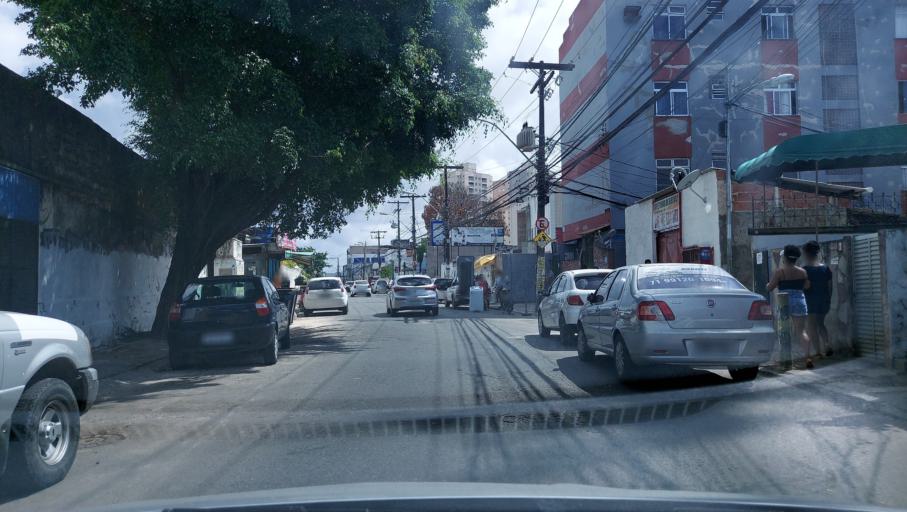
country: BR
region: Bahia
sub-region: Salvador
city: Salvador
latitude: -12.9878
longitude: -38.4780
